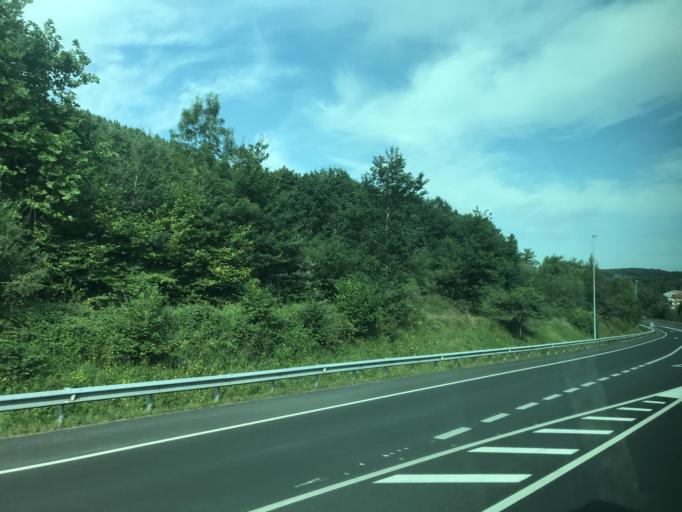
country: ES
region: Basque Country
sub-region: Bizkaia
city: Otxandio
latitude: 43.0348
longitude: -2.6500
